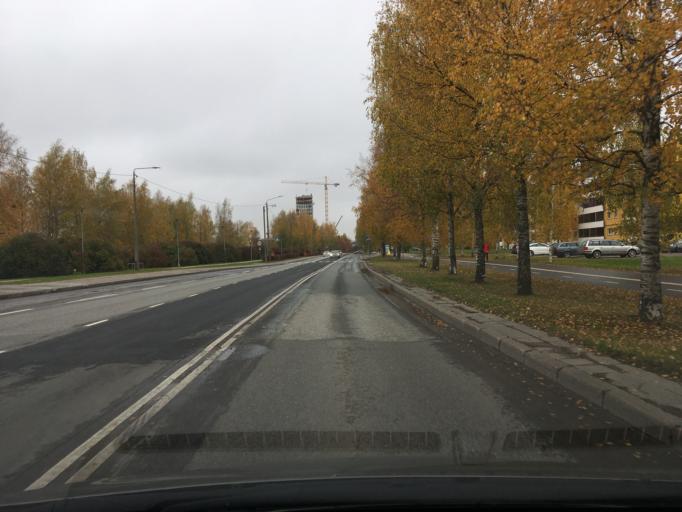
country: EE
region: Tartu
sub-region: Tartu linn
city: Tartu
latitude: 58.3758
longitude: 26.7463
